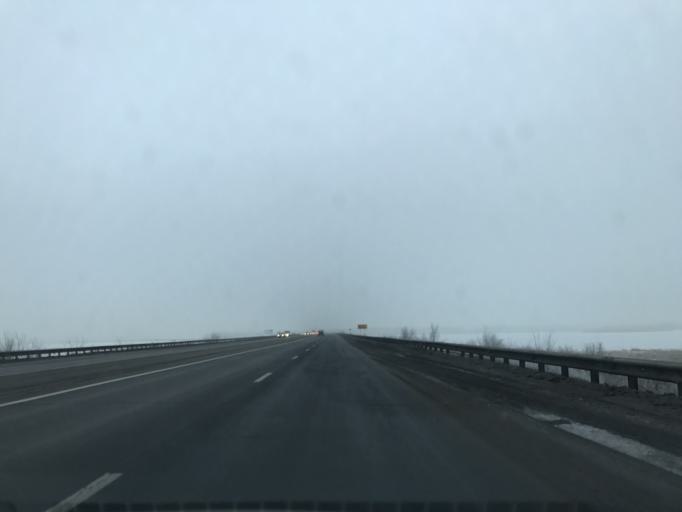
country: RU
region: Rostov
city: Grushevskaya
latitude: 47.4504
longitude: 39.9743
